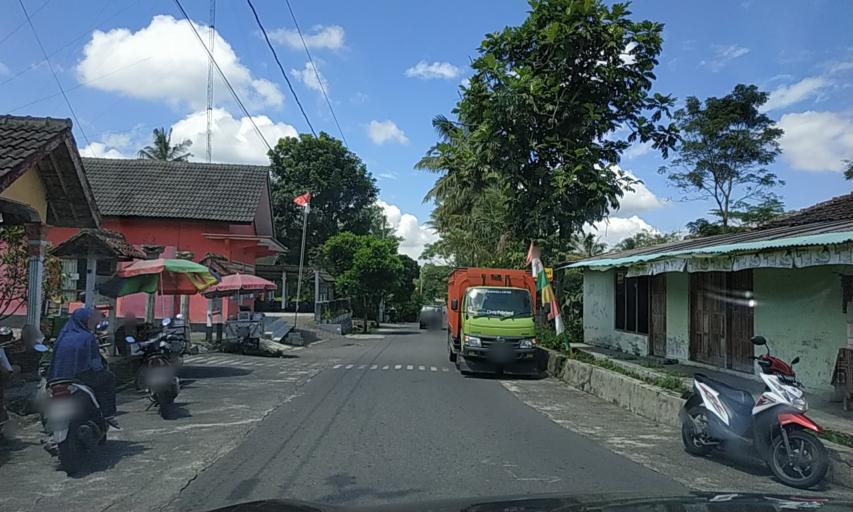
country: ID
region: Central Java
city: Muntilan
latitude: -7.5519
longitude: 110.3397
